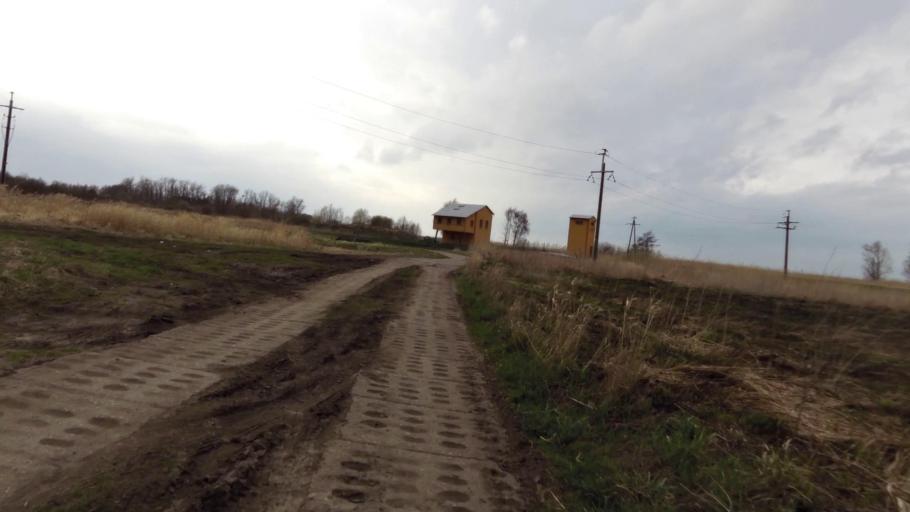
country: PL
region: West Pomeranian Voivodeship
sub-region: Koszalin
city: Koszalin
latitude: 54.2727
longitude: 16.1926
